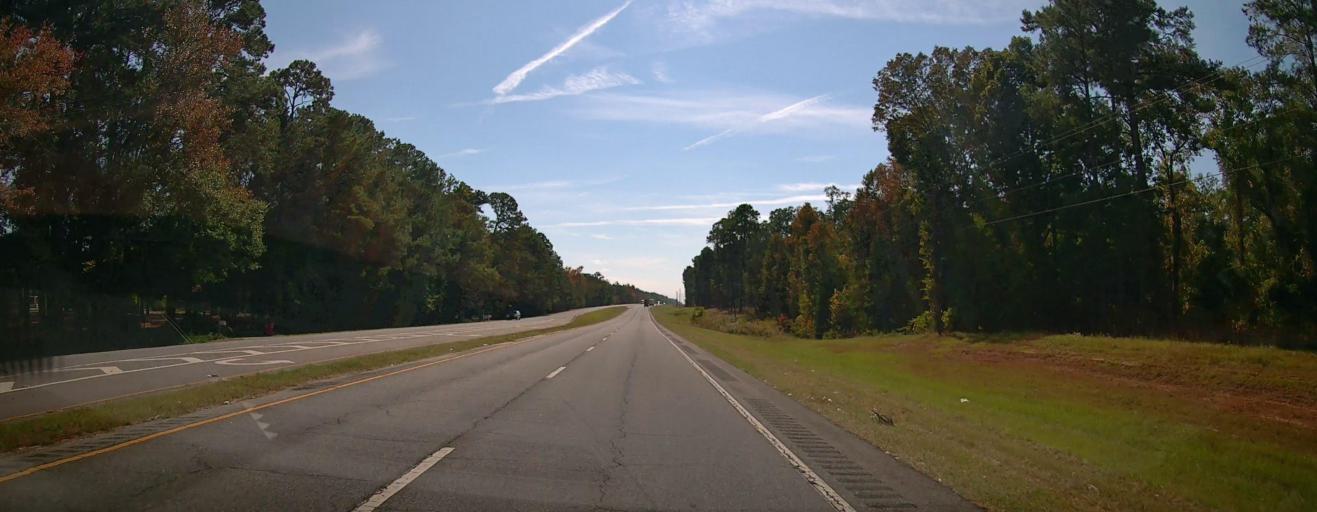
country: US
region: Georgia
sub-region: Lee County
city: Leesburg
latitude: 31.8030
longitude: -83.9557
